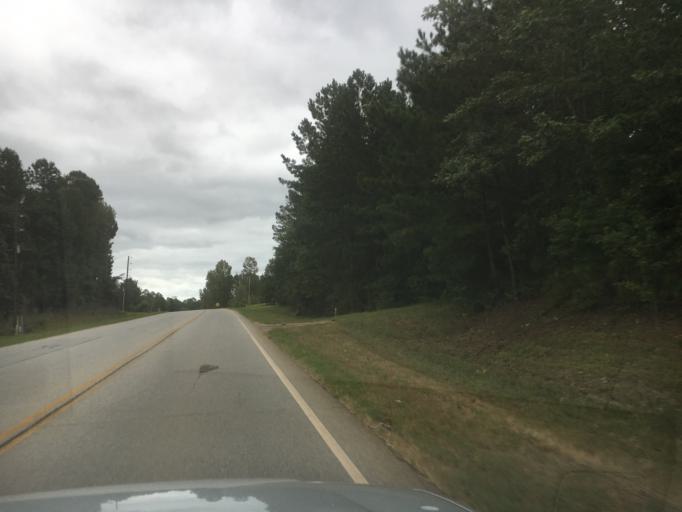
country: US
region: Georgia
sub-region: Lincoln County
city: Lincolnton
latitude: 33.7464
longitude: -82.5233
